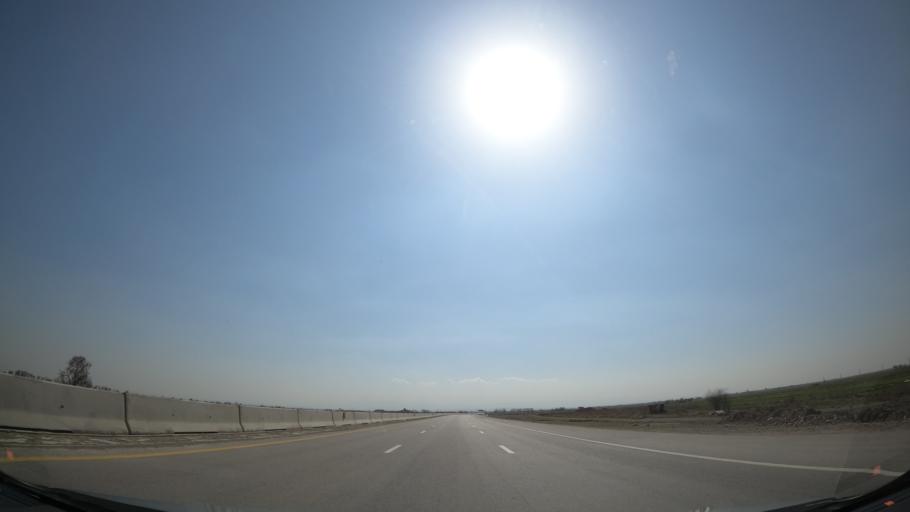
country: IR
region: Qazvin
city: Abyek
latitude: 35.9887
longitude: 50.4621
